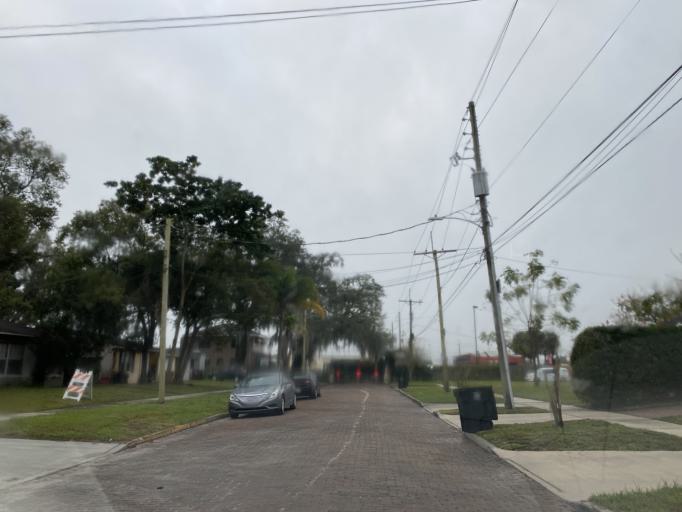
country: US
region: Florida
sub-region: Orange County
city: Orlando
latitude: 28.5544
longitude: -81.3948
